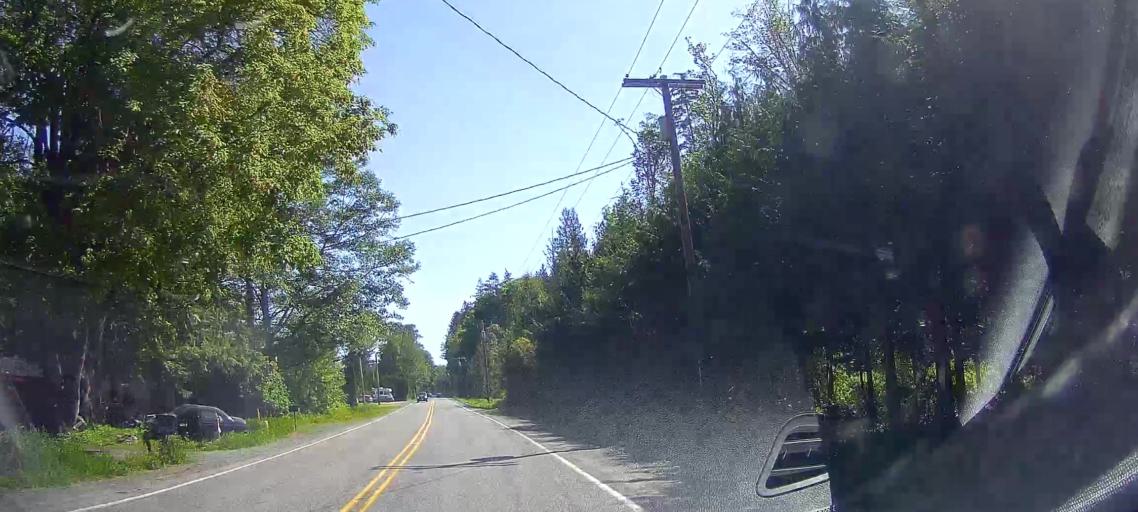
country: US
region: Washington
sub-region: Skagit County
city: Sedro-Woolley
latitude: 48.4871
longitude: -122.2184
